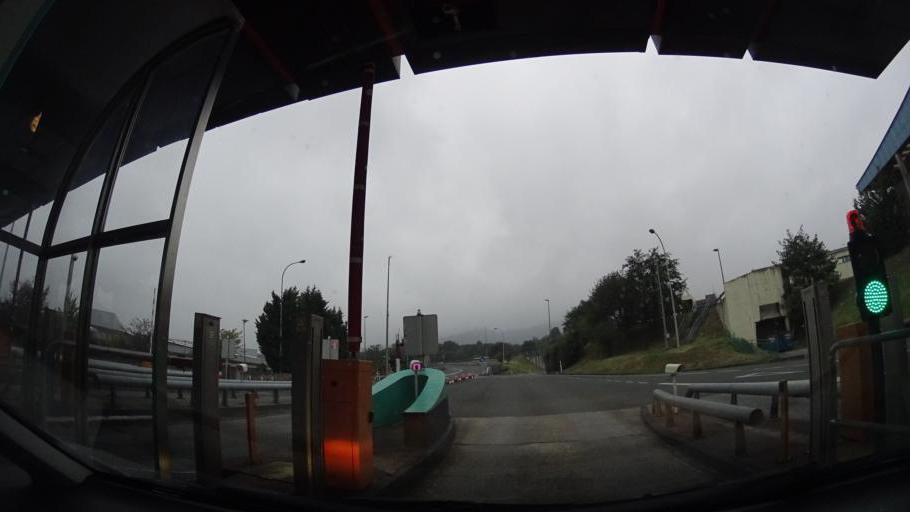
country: ES
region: Basque Country
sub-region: Bizkaia
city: Iurreta
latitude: 43.1786
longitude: -2.6430
